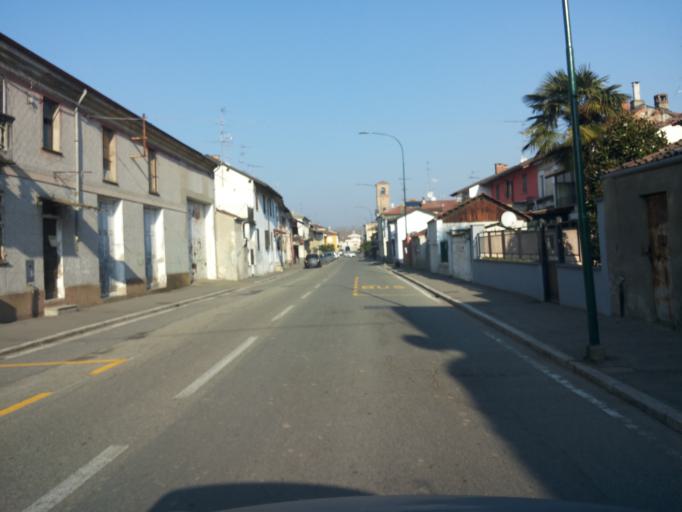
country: IT
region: Piedmont
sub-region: Provincia di Vercelli
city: Caresana
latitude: 45.2190
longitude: 8.5064
